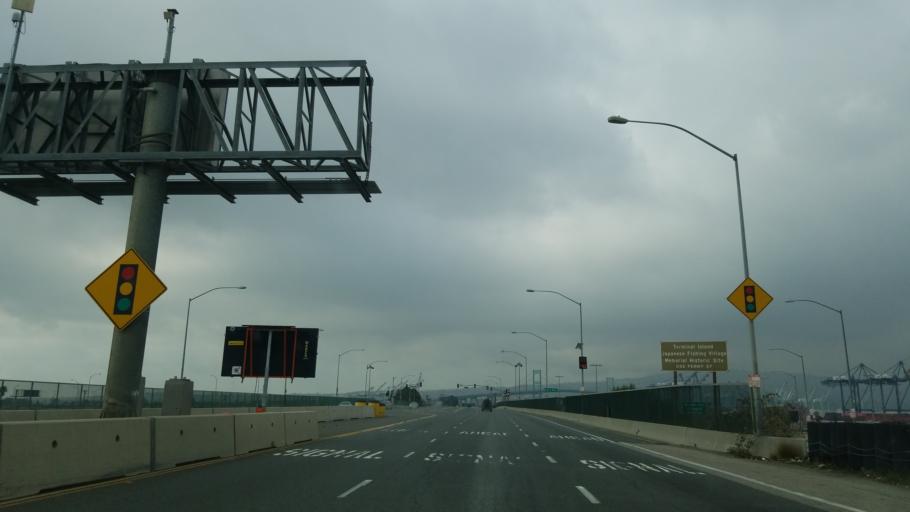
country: US
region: California
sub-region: Los Angeles County
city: San Pedro
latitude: 33.7550
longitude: -118.2494
